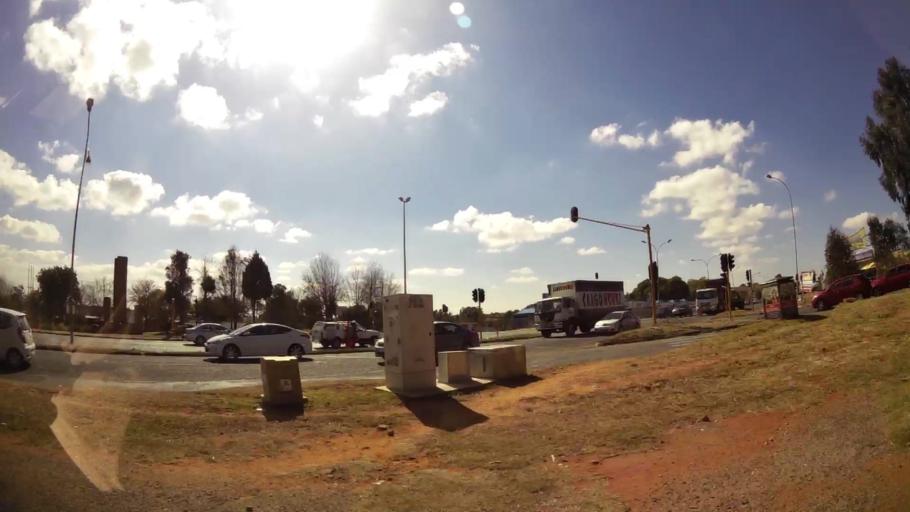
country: ZA
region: Gauteng
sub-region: City of Johannesburg Metropolitan Municipality
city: Roodepoort
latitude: -26.1273
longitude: 27.8394
